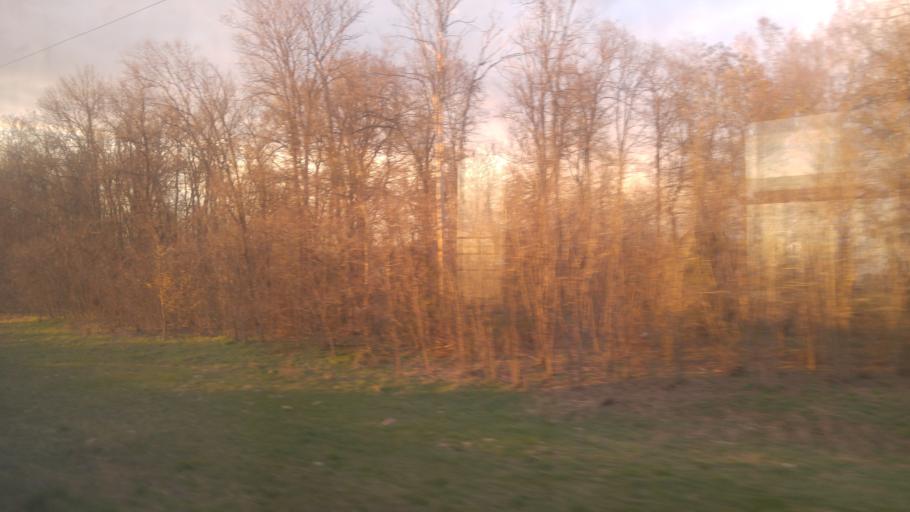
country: BY
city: Michanovichi
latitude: 53.6596
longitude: 27.7630
